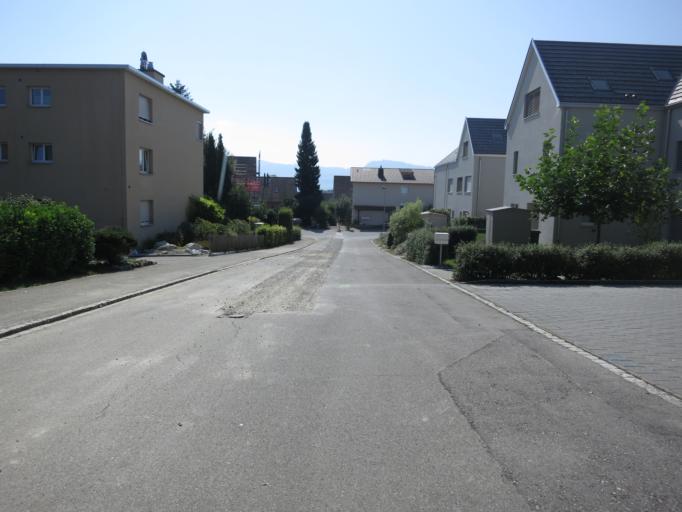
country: CH
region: Zurich
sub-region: Bezirk Meilen
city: Hombrechtikon
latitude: 47.2553
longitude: 8.7664
